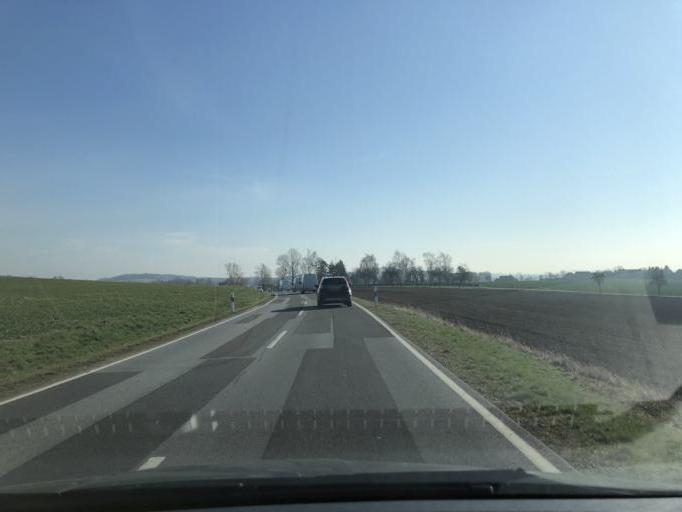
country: DE
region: Saxony
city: Frankenthal
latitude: 51.1505
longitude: 14.1134
